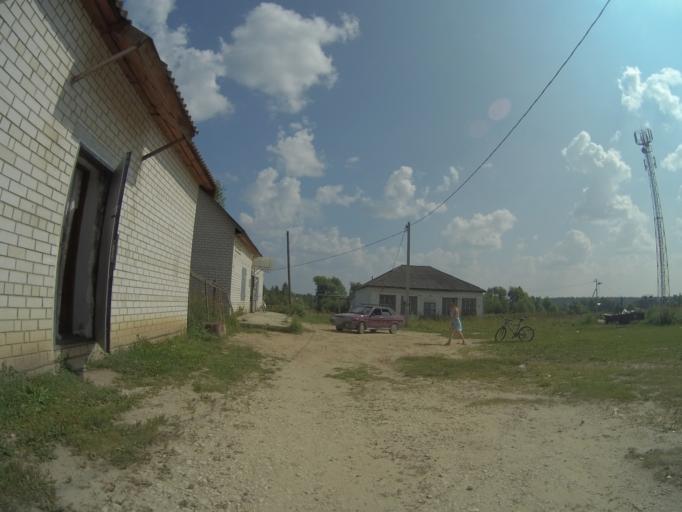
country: RU
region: Vladimir
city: Imeni Vorovskogo
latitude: 55.7240
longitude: 41.1213
